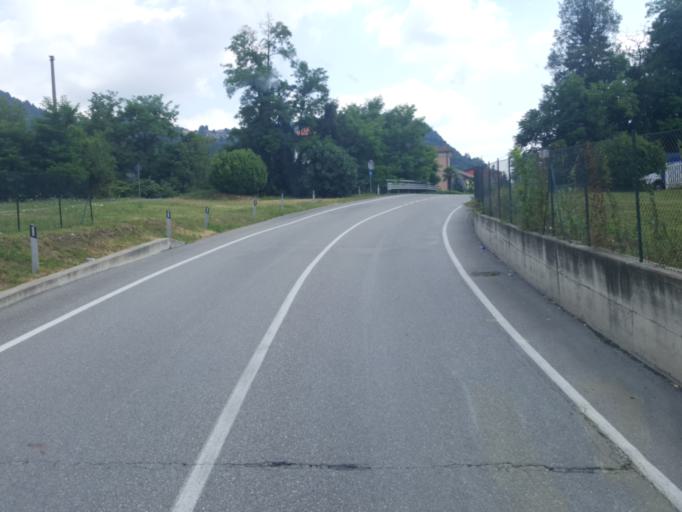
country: IT
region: Lombardy
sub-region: Provincia di Lecco
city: Calolziocorte
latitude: 45.7859
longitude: 9.4412
